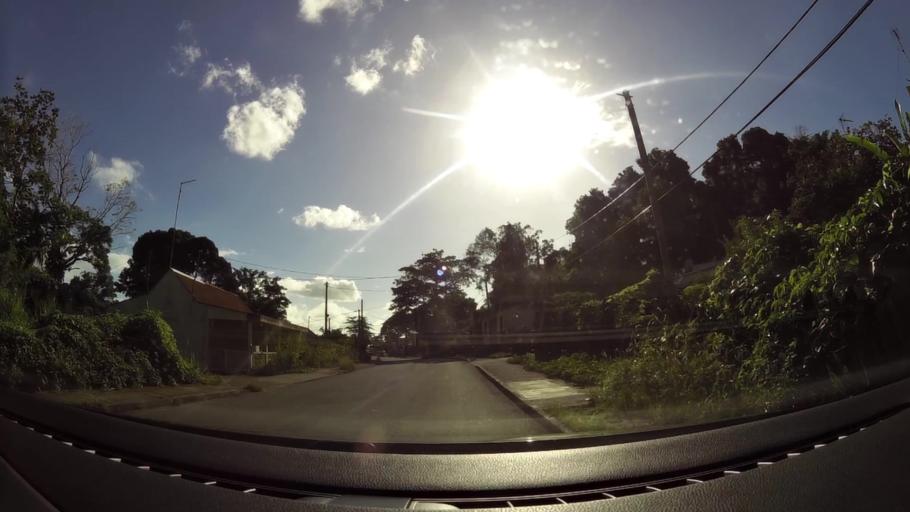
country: GP
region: Guadeloupe
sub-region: Guadeloupe
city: Petit-Canal
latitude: 16.3253
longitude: -61.4456
